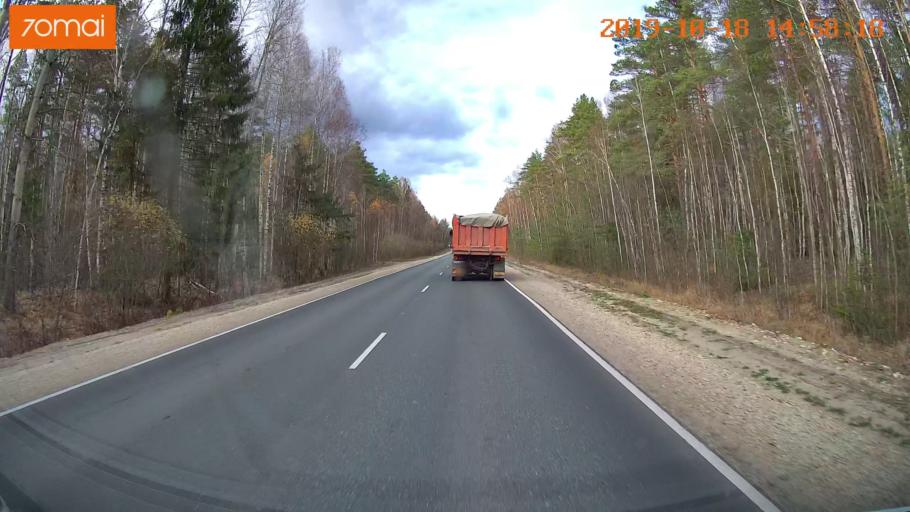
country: RU
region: Vladimir
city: Kurlovo
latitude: 55.4890
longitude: 40.5777
